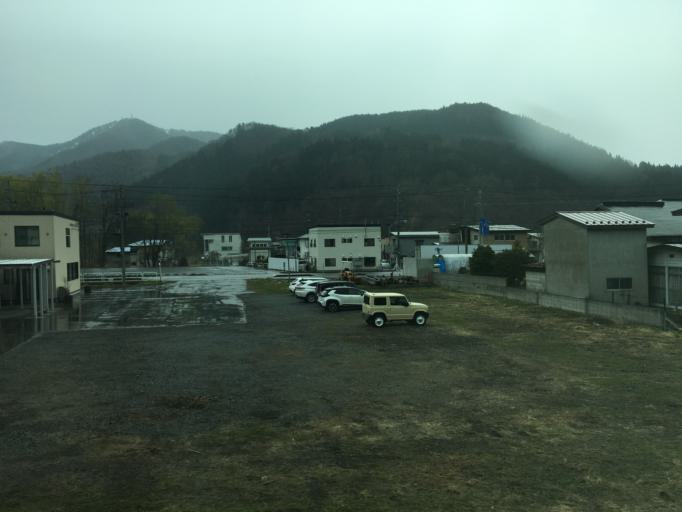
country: JP
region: Aomori
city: Kuroishi
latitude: 40.5208
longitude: 140.5894
